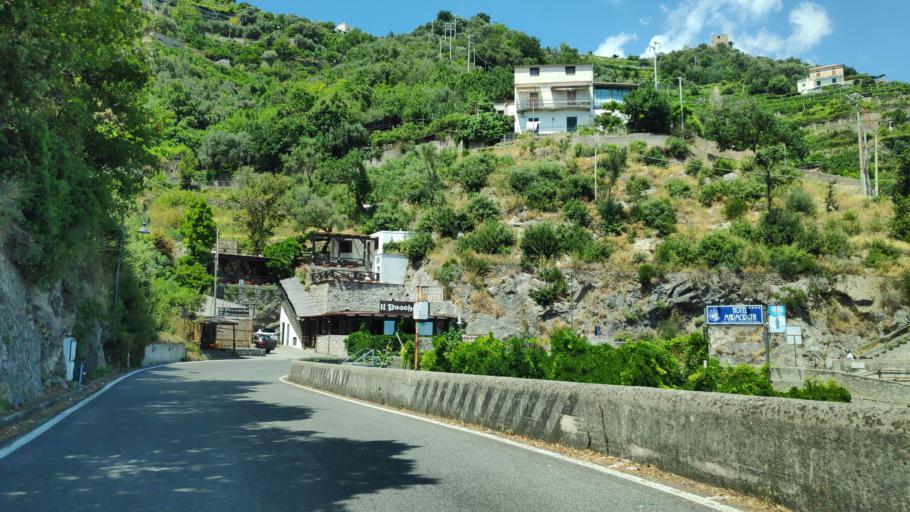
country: IT
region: Campania
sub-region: Provincia di Salerno
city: Ravello
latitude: 40.6457
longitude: 14.6188
